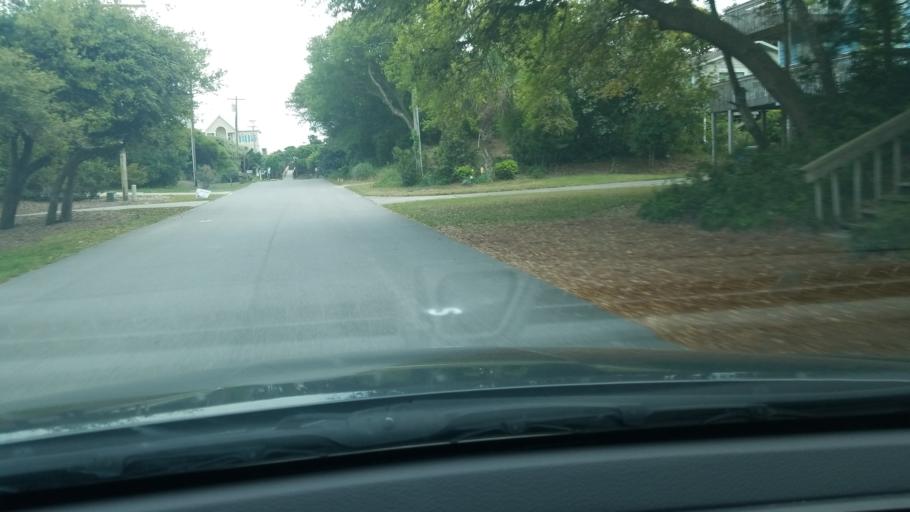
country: US
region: North Carolina
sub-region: Carteret County
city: Cape Carteret
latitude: 34.6666
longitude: -77.0167
